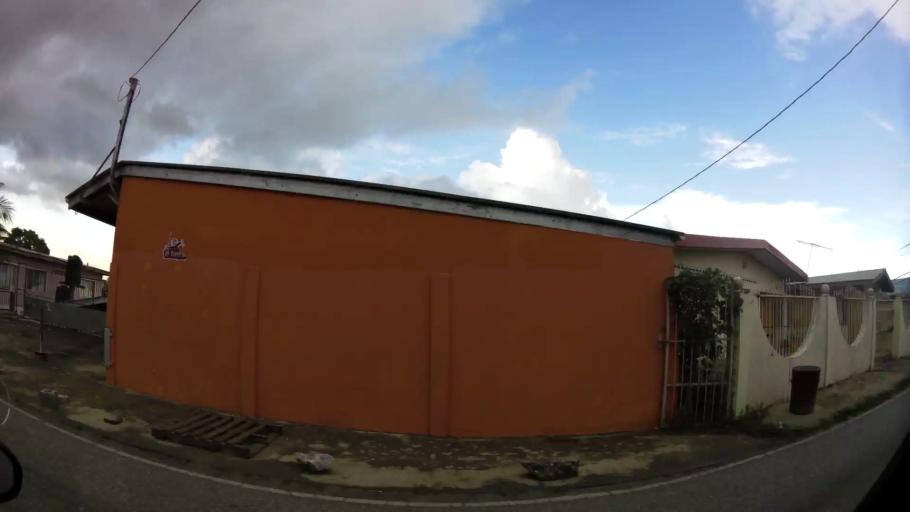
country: TT
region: City of San Fernando
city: Mon Repos
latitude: 10.2445
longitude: -61.4515
